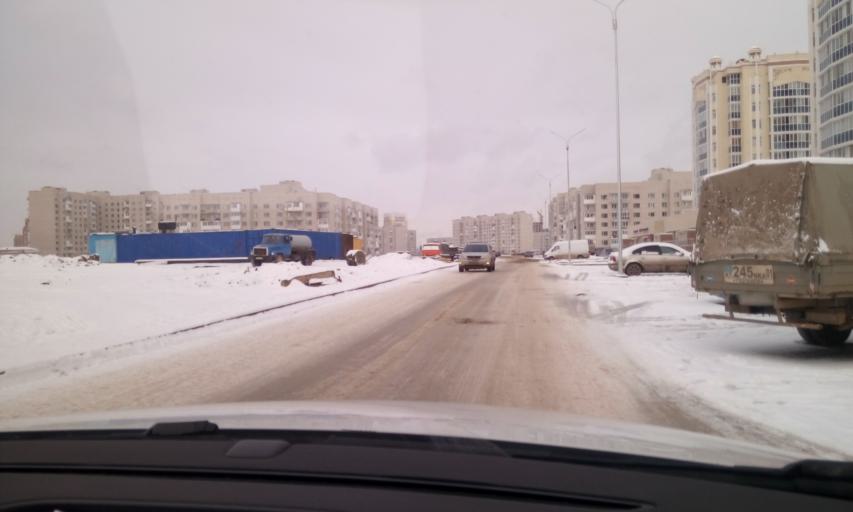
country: KZ
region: Astana Qalasy
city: Astana
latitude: 51.1205
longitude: 71.5037
